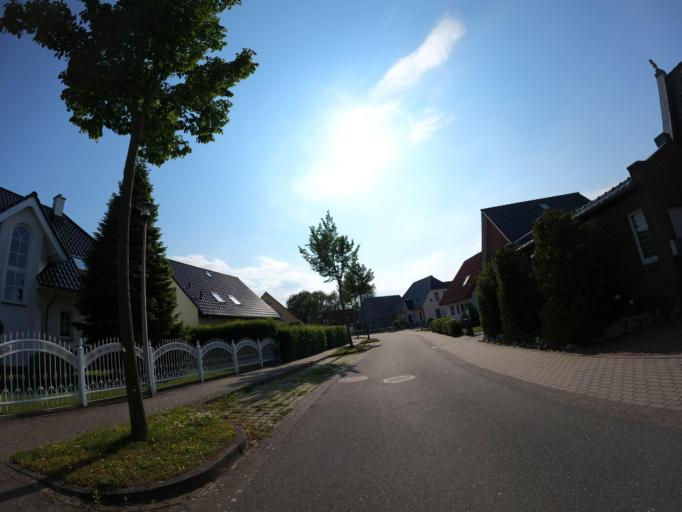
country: DE
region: Mecklenburg-Vorpommern
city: Stralsund
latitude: 54.2943
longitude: 13.0702
